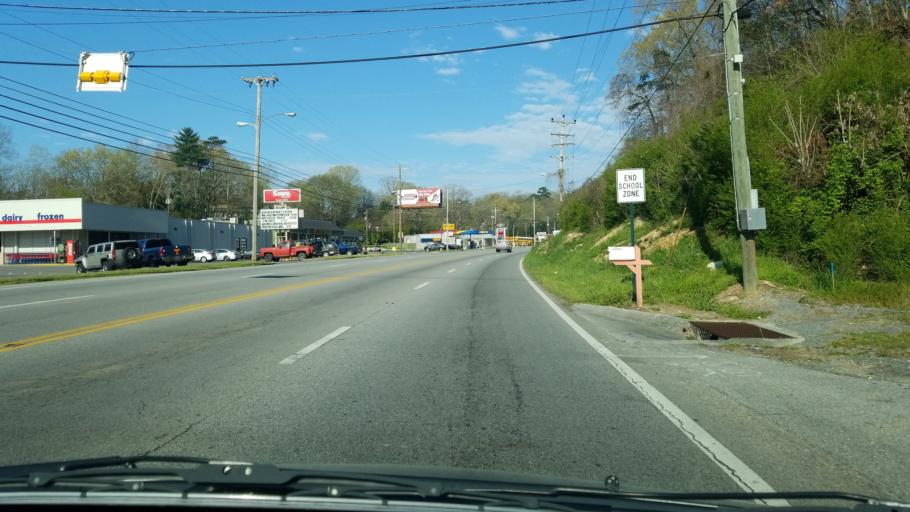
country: US
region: Tennessee
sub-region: Hamilton County
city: East Ridge
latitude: 34.9977
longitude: -85.2515
